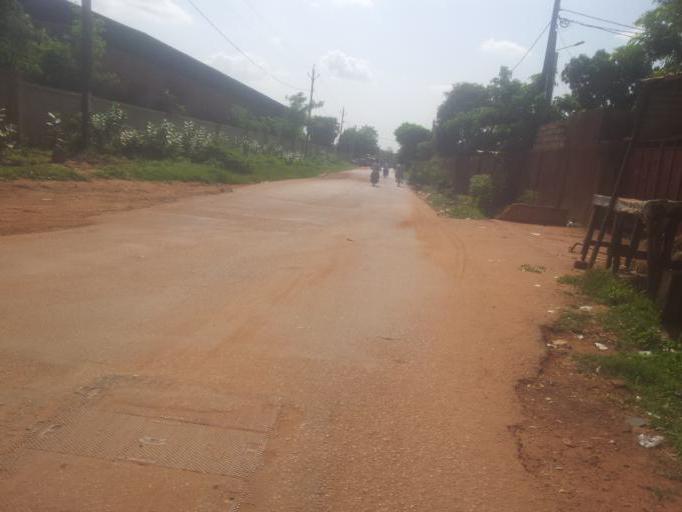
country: BF
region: Centre
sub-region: Kadiogo Province
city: Ouagadougou
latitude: 12.3625
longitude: -1.5419
